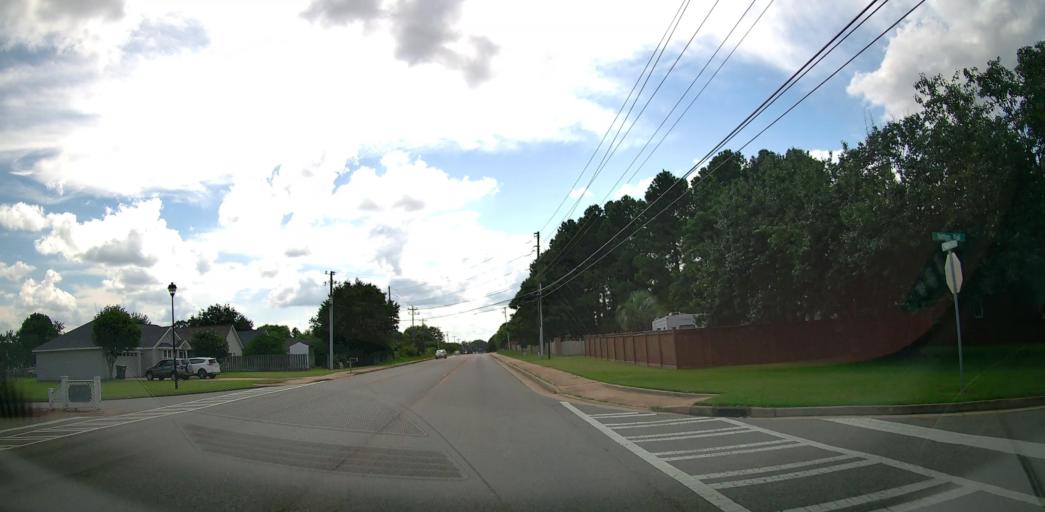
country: US
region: Georgia
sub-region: Houston County
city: Centerville
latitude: 32.5710
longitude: -83.6809
